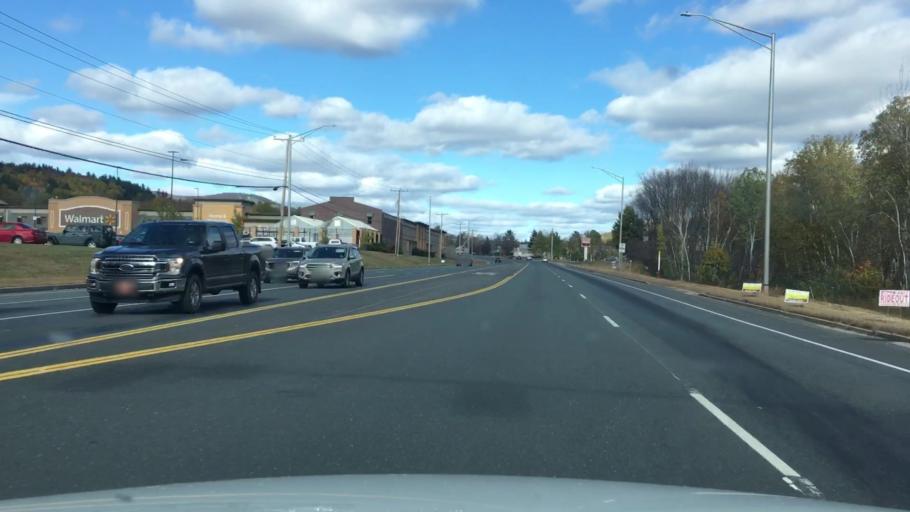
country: US
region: New Hampshire
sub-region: Coos County
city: Gorham
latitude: 44.4245
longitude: -71.1935
